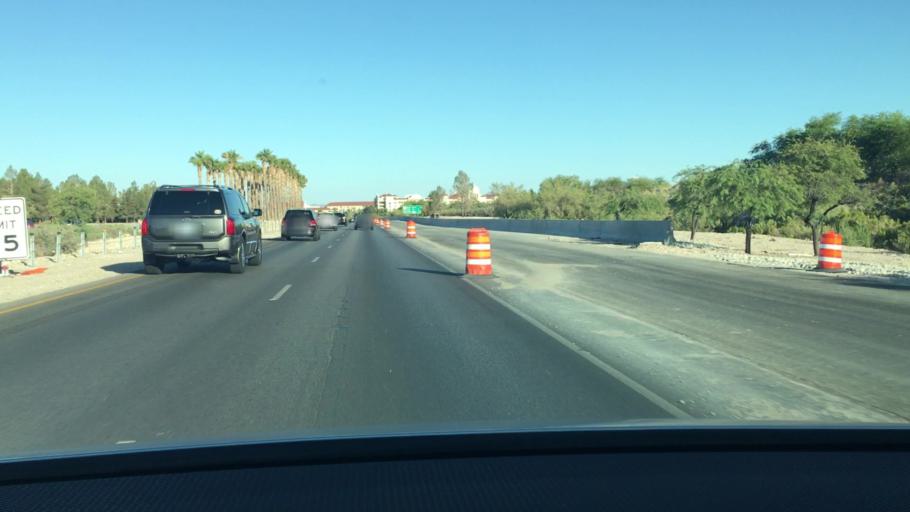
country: US
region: Nevada
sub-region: Clark County
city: Summerlin South
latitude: 36.1818
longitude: -115.3000
